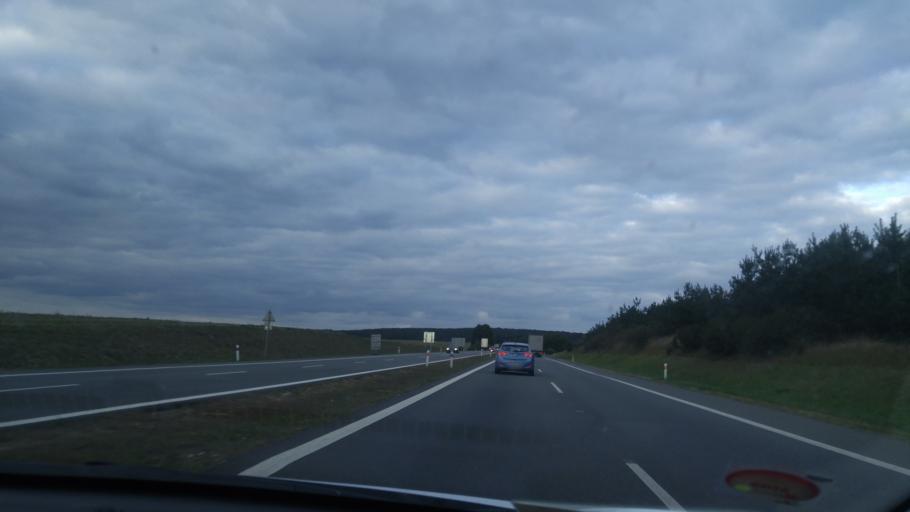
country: CZ
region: South Moravian
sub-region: Okres Brno-Venkov
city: Rosice
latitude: 49.1875
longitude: 16.4165
